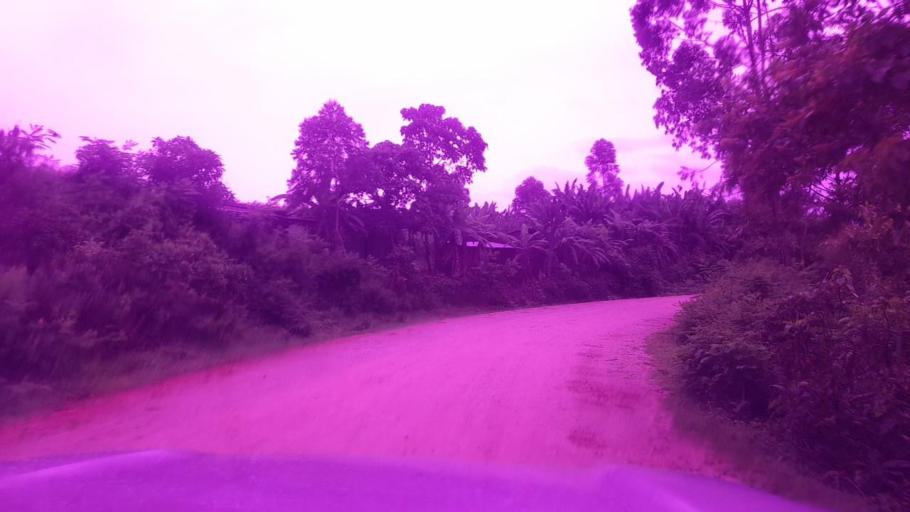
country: ET
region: Southern Nations, Nationalities, and People's Region
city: Bonga
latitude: 7.4527
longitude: 36.1278
